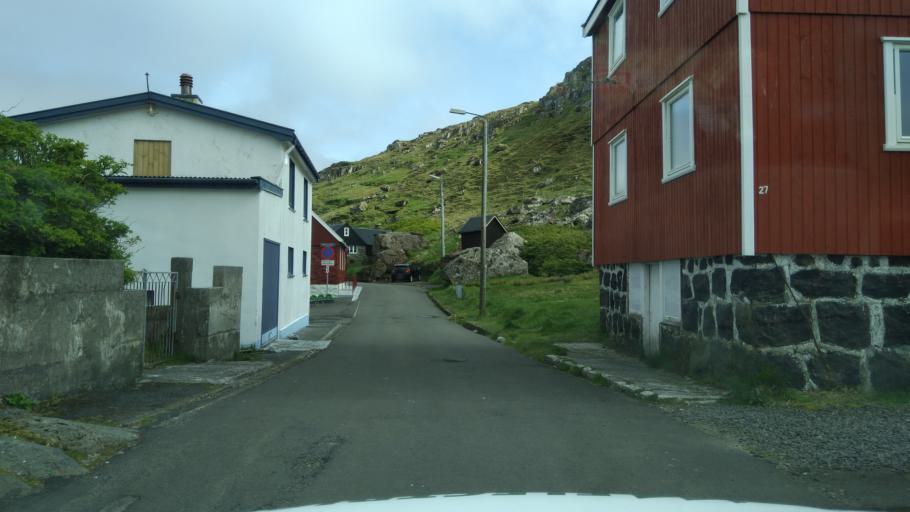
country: FO
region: Sandoy
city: Sandur
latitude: 61.9024
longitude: -6.8847
